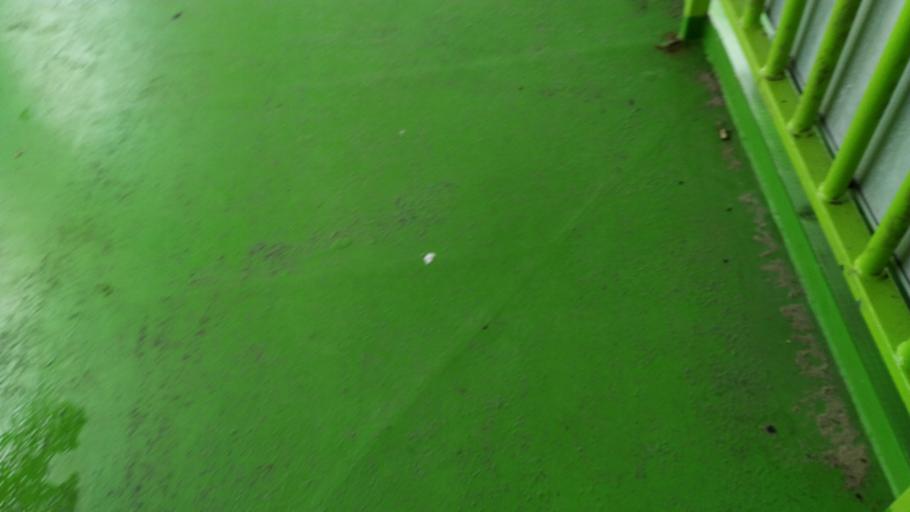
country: PT
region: Setubal
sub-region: Setubal
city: Setubal
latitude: 38.5186
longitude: -8.8856
